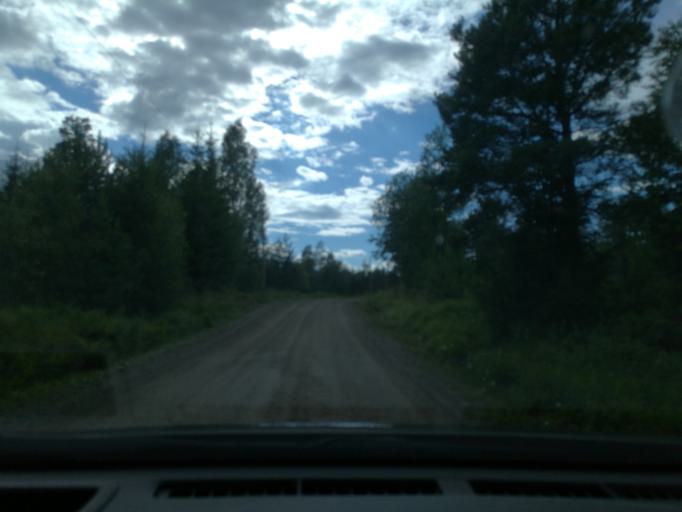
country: SE
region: Vaestmanland
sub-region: Surahammars Kommun
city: Ramnas
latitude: 59.8207
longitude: 16.2640
